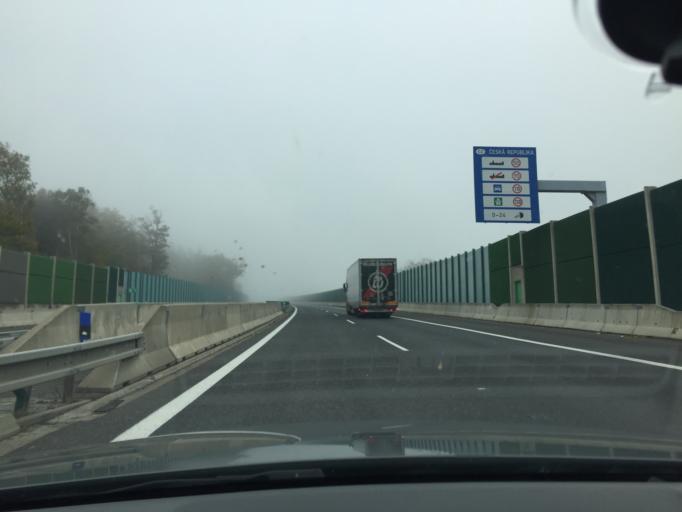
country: CZ
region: Ustecky
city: Chlumec
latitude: 50.7796
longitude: 13.9090
